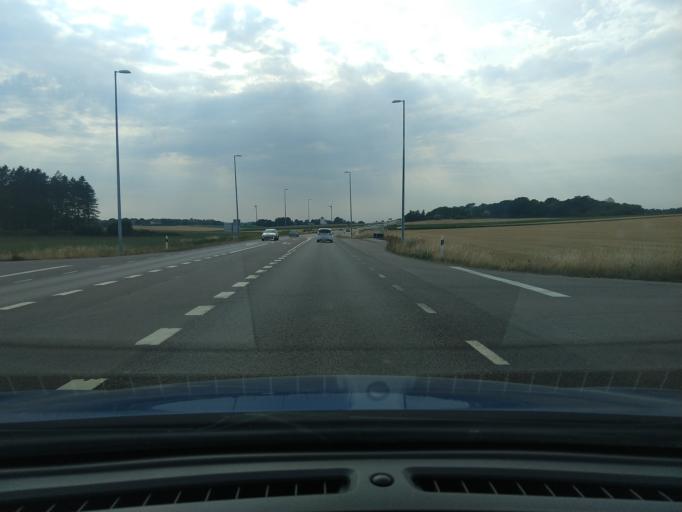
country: SE
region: Blekinge
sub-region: Karlskrona Kommun
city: Jaemjoe
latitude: 56.1845
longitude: 15.7917
